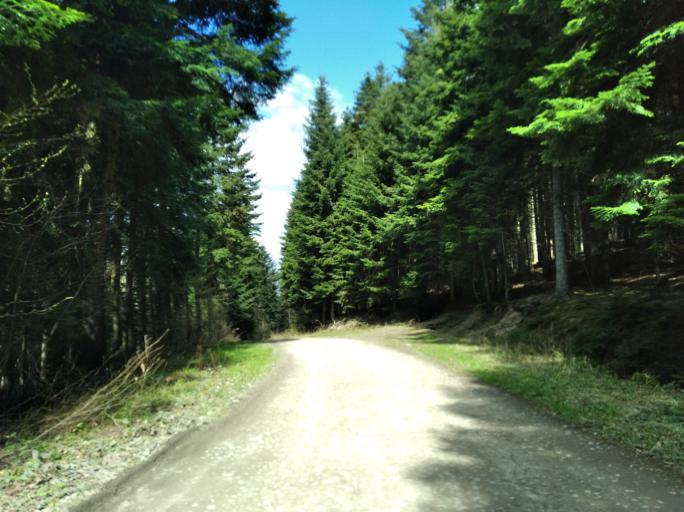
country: PL
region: Subcarpathian Voivodeship
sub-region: Powiat strzyzowski
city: Wysoka Strzyzowska
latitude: 49.8299
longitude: 21.7696
